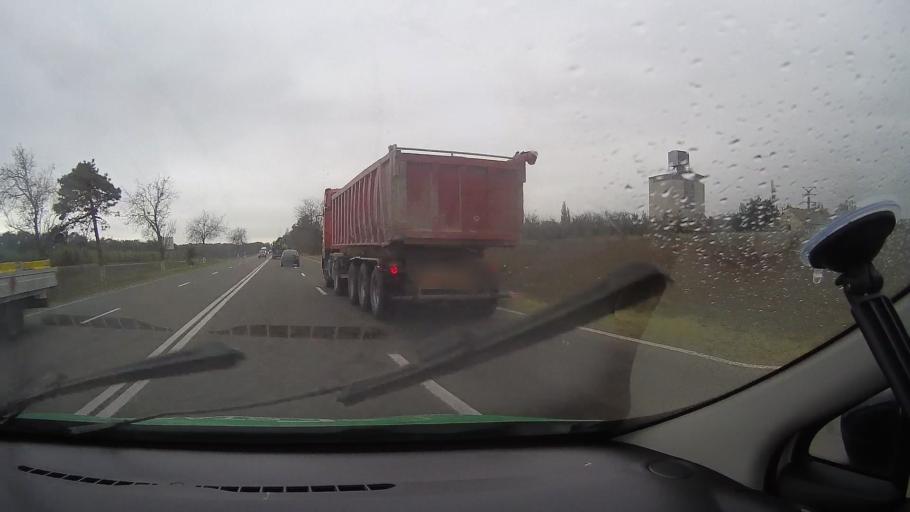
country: RO
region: Constanta
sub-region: Comuna Valu lui Traian
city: Valu lui Traian
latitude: 44.1655
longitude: 28.5143
